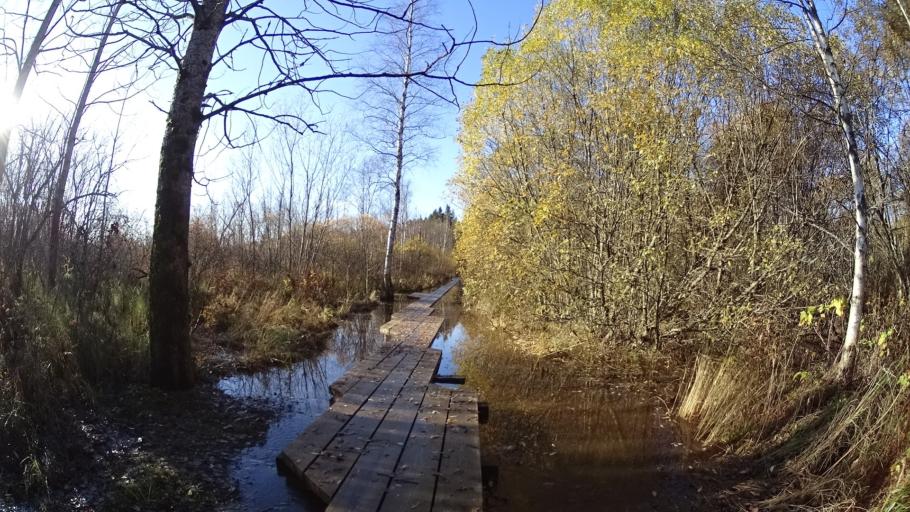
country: FI
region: Uusimaa
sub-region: Helsinki
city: Kilo
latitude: 60.2827
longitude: 24.7906
